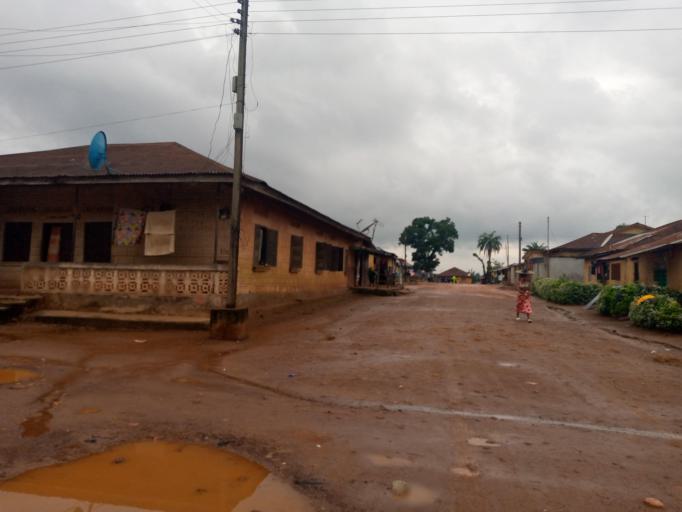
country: SL
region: Eastern Province
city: Kenema
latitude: 7.8810
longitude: -11.1850
